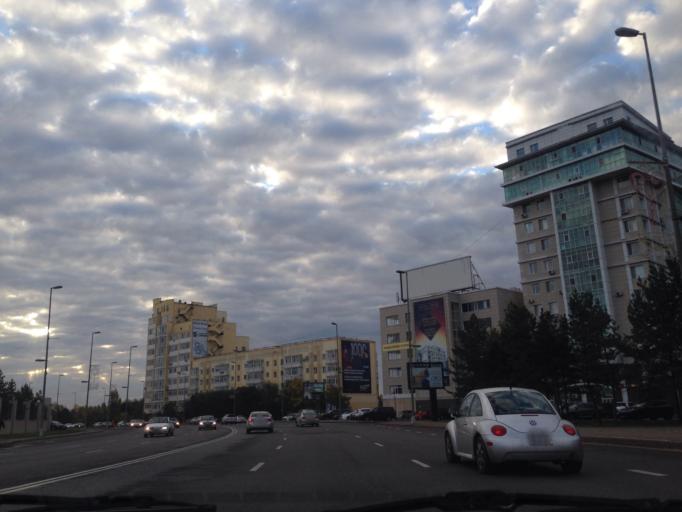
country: KZ
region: Astana Qalasy
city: Astana
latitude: 51.1528
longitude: 71.4337
